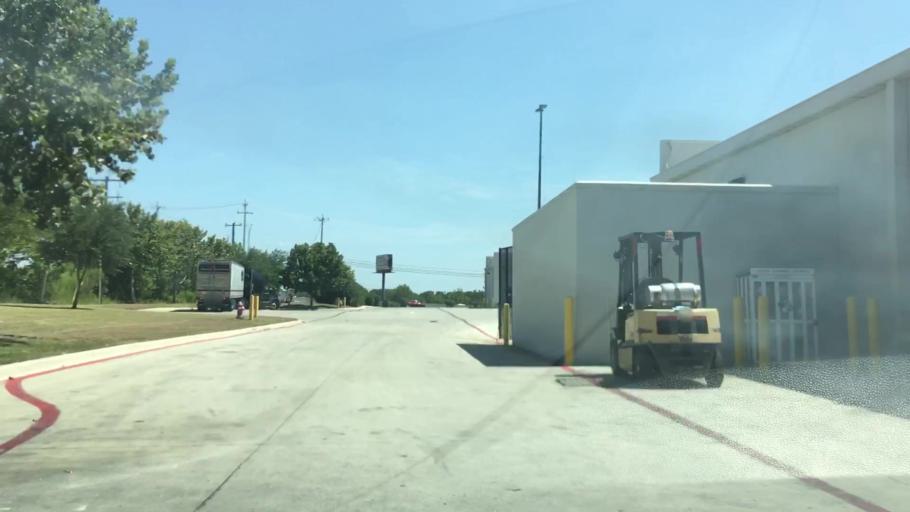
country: US
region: Texas
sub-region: Bexar County
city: Selma
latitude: 29.6046
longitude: -98.2745
